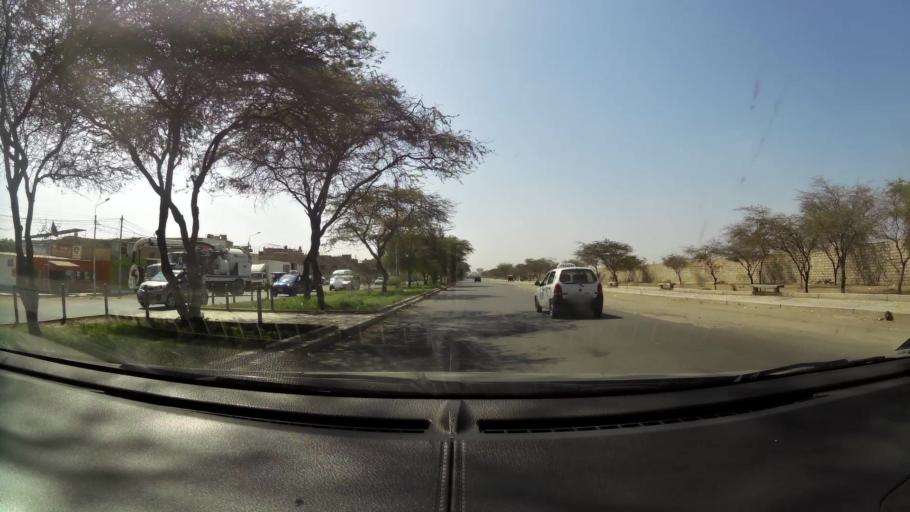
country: PE
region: Lambayeque
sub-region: Provincia de Chiclayo
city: Chiclayo
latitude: -6.7973
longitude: -79.8308
